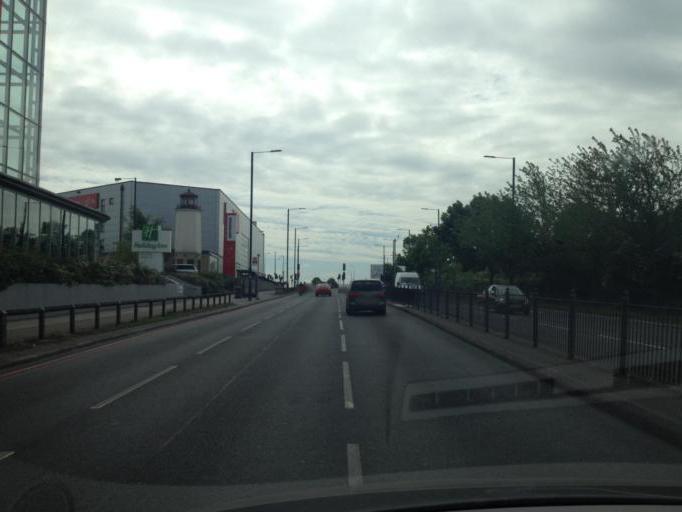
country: GB
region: England
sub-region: Greater London
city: Acton
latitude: 51.5211
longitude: -0.2633
